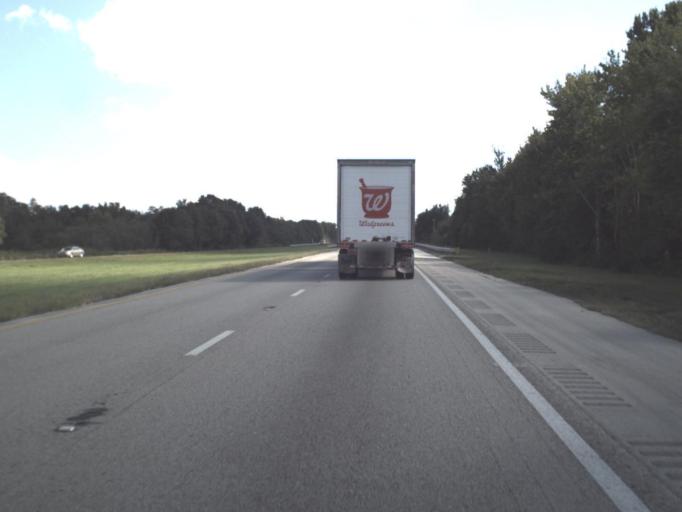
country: US
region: Florida
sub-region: Osceola County
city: Saint Cloud
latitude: 28.0516
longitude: -81.2207
